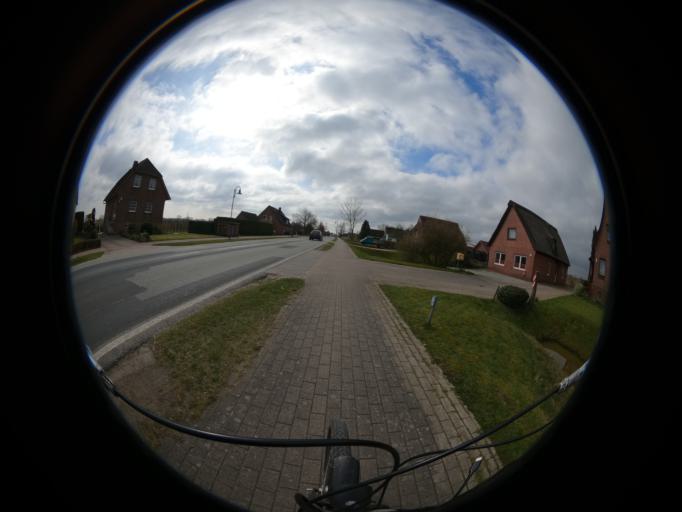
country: DE
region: Lower Saxony
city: Neu Wulmstorf
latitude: 53.4970
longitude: 9.7802
